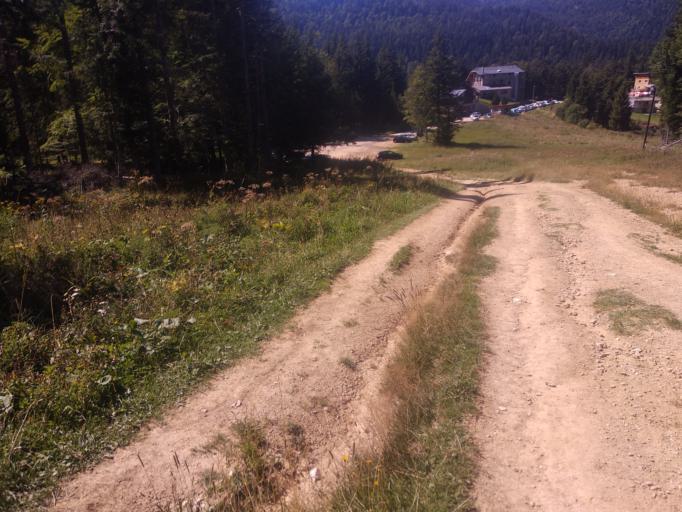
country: FR
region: Rhone-Alpes
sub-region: Departement de l'Isere
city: Le Sappey-en-Chartreuse
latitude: 45.2884
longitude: 5.7696
